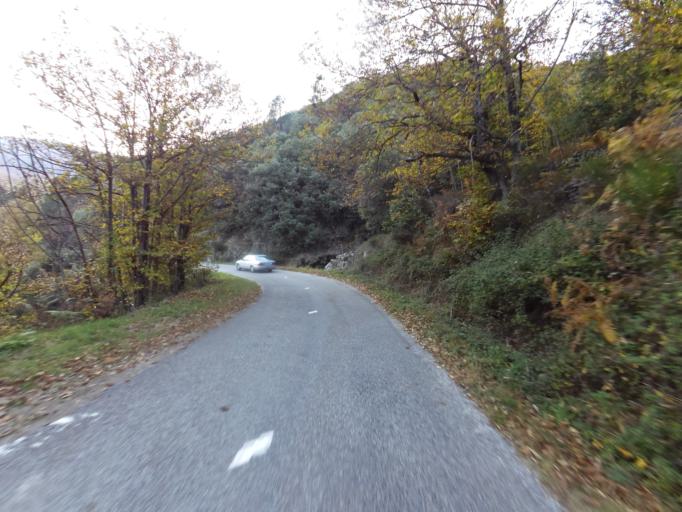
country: FR
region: Rhone-Alpes
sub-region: Departement de l'Ardeche
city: Les Vans
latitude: 44.5345
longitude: 4.0627
